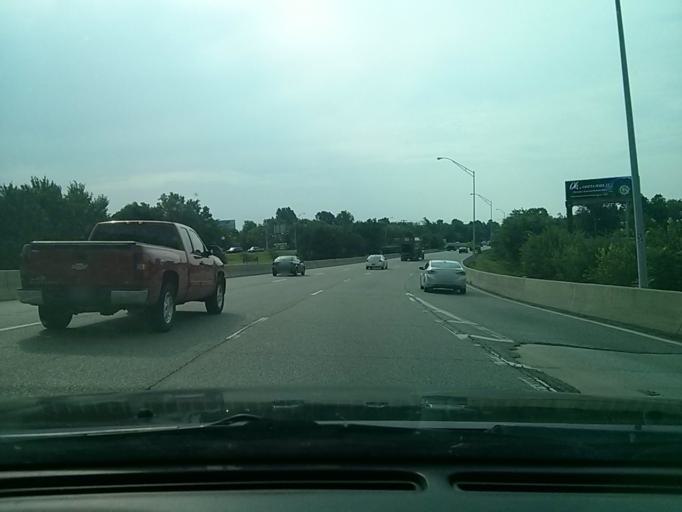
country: US
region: Oklahoma
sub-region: Tulsa County
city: Tulsa
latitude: 36.1420
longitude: -95.9561
